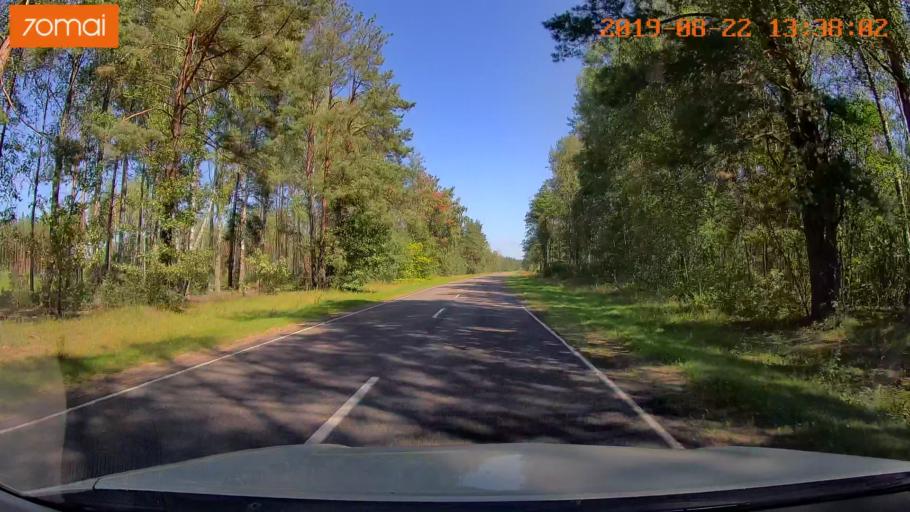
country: BY
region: Minsk
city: Staryya Darohi
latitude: 53.2204
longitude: 28.3127
